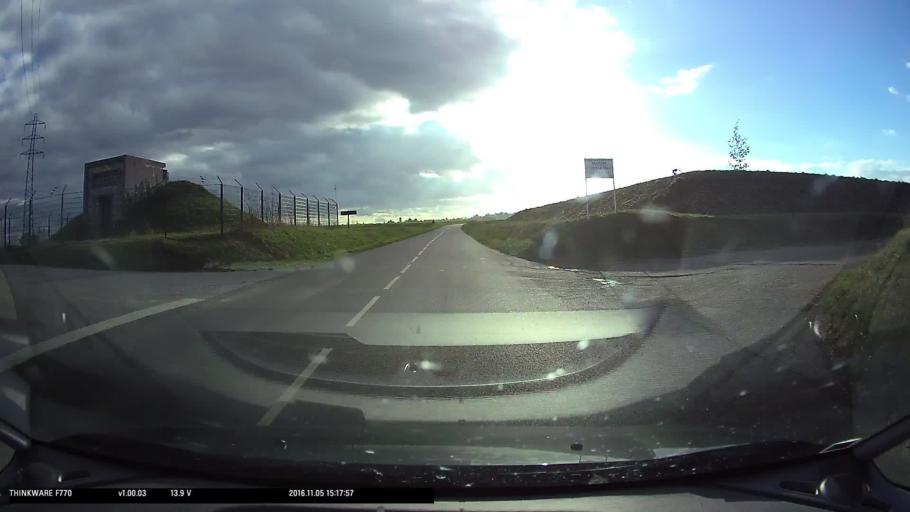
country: FR
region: Ile-de-France
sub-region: Departement du Val-d'Oise
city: Ableiges
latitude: 49.0814
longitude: 1.9769
